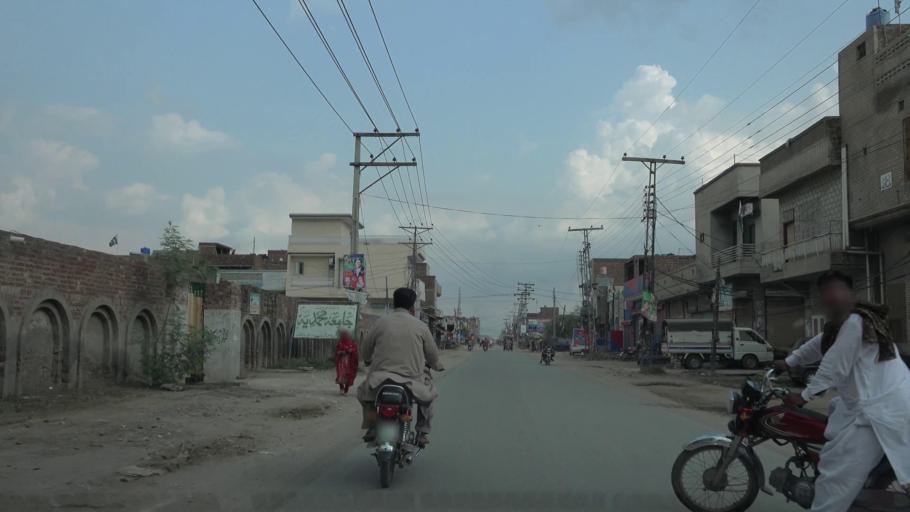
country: PK
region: Punjab
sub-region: Nankana Sahib District
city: Shahkot
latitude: 31.5714
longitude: 73.4869
